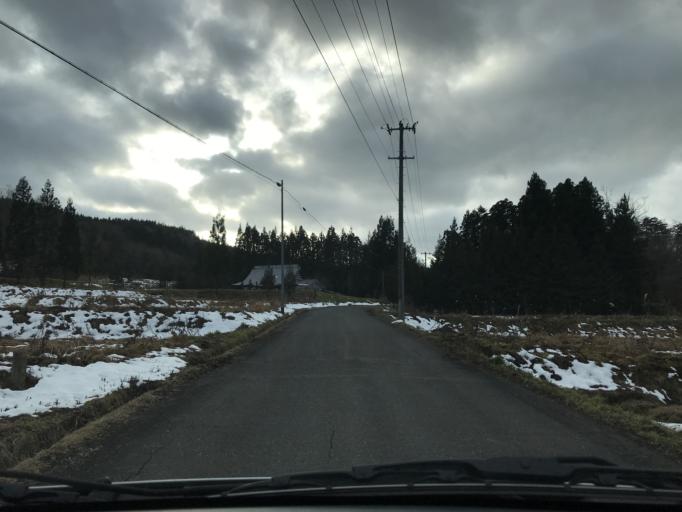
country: JP
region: Iwate
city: Ichinoseki
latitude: 38.9974
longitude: 140.9997
